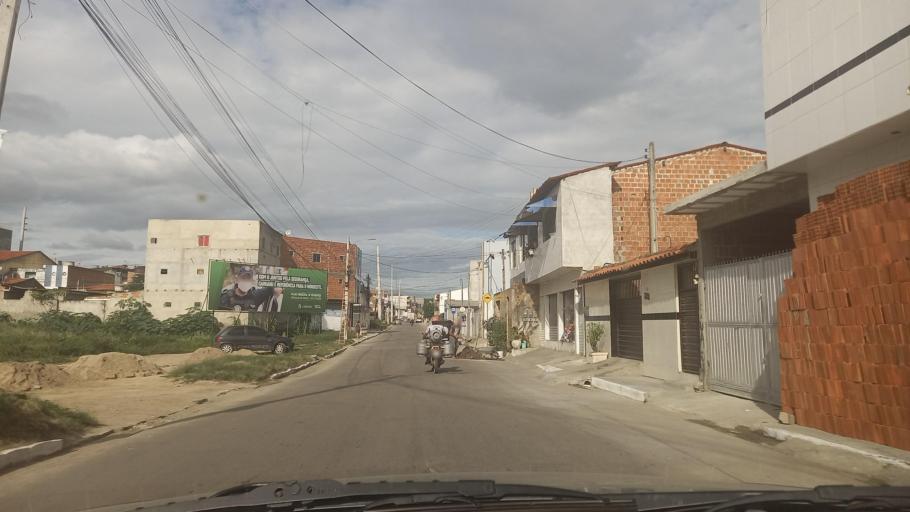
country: BR
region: Pernambuco
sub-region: Caruaru
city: Caruaru
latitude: -8.2850
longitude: -35.9949
